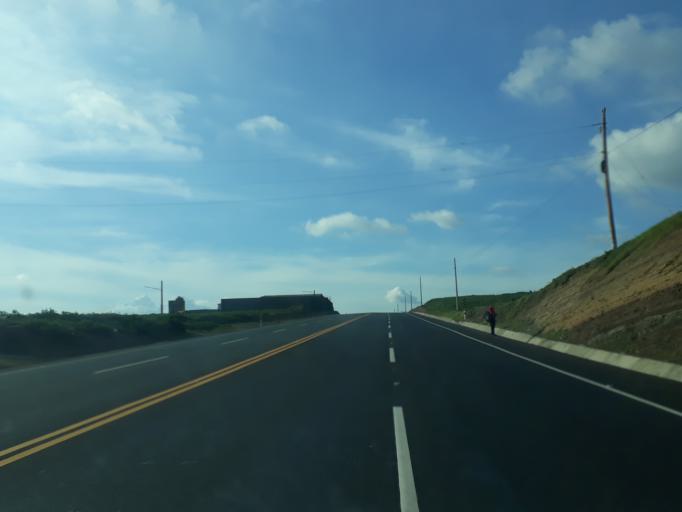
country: NI
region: Managua
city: El Crucero
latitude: 11.9425
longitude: -86.2977
